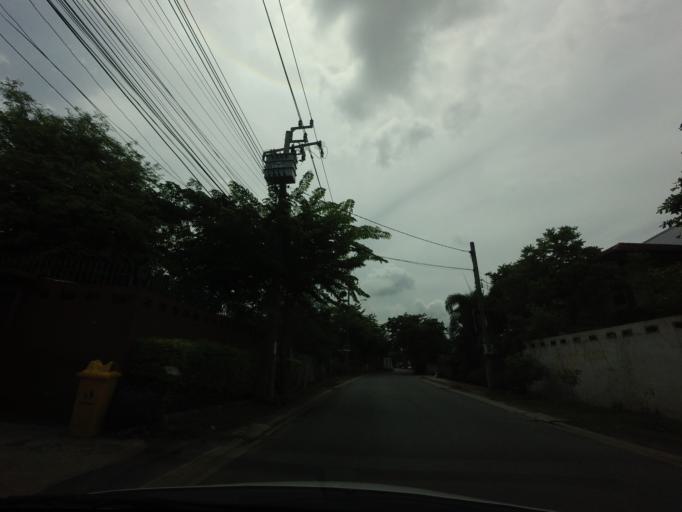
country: TH
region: Bangkok
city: Thung Khru
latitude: 13.6443
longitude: 100.5093
